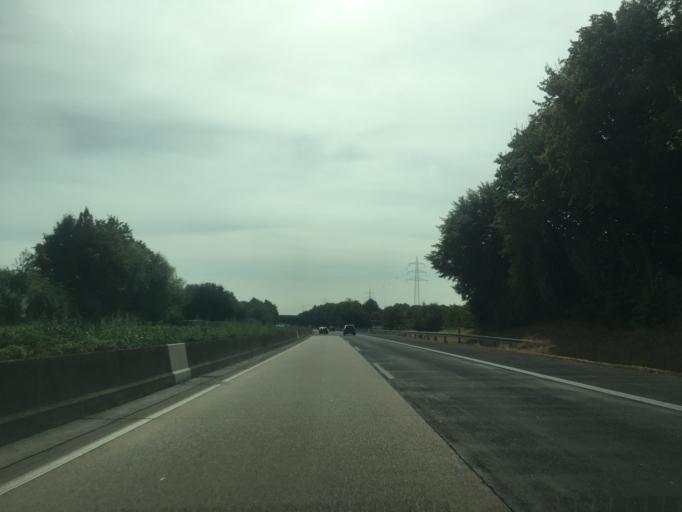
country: DE
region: North Rhine-Westphalia
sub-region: Regierungsbezirk Koln
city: Bedburg
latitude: 50.9710
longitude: 6.5627
